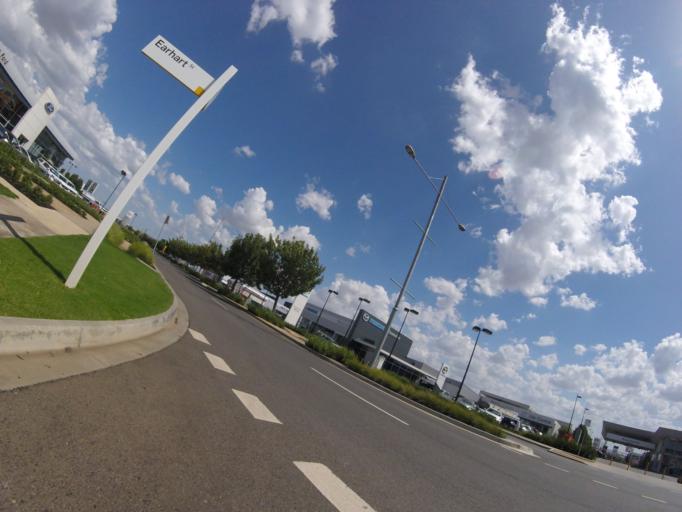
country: AU
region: Victoria
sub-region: Moreland
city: Gowanbrae
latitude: -37.7173
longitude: 144.8950
